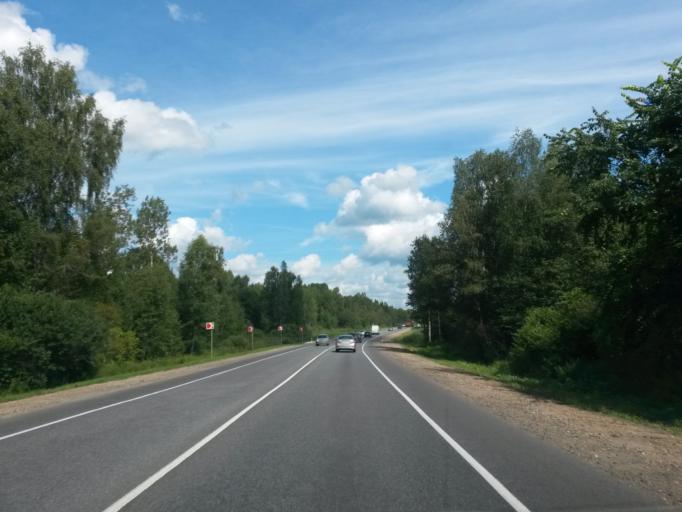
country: RU
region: Jaroslavl
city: Pereslavl'-Zalesskiy
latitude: 56.8205
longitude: 38.9054
